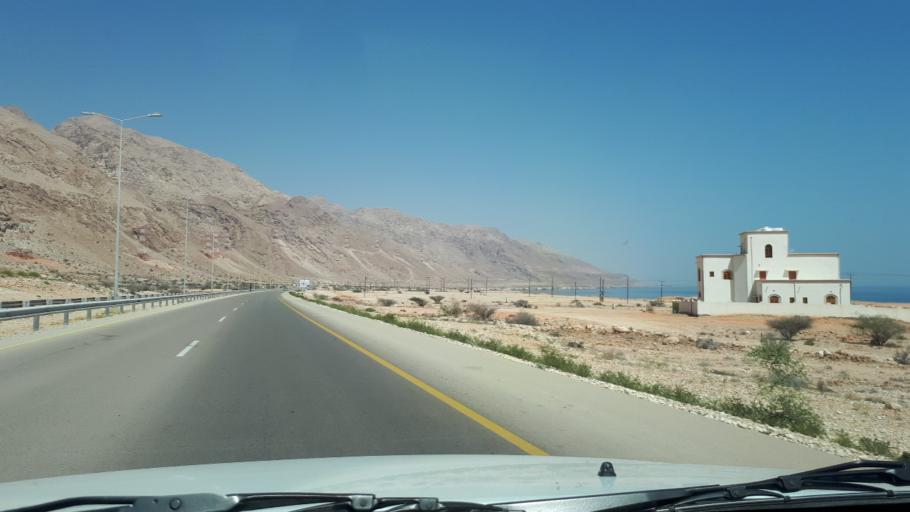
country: OM
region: Ash Sharqiyah
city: Sur
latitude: 22.7508
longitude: 59.3091
